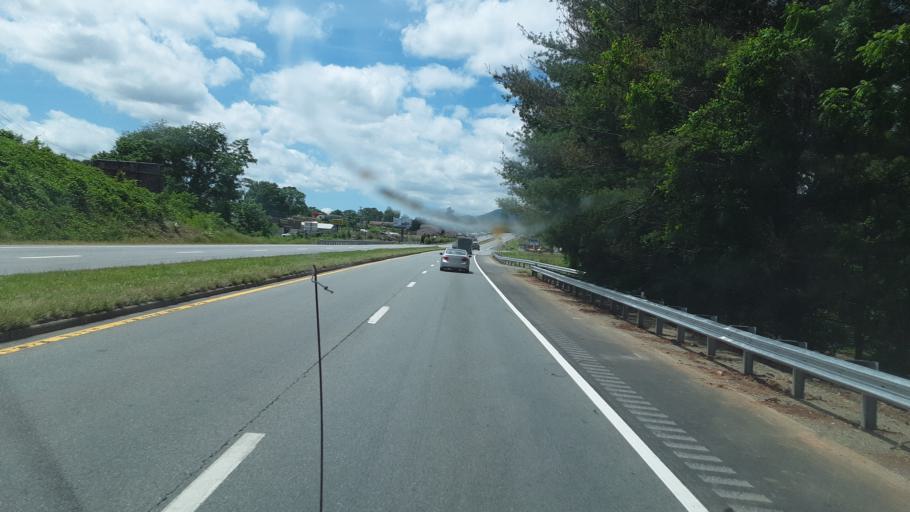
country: US
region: Virginia
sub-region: Franklin County
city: Rocky Mount
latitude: 37.0746
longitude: -79.9096
